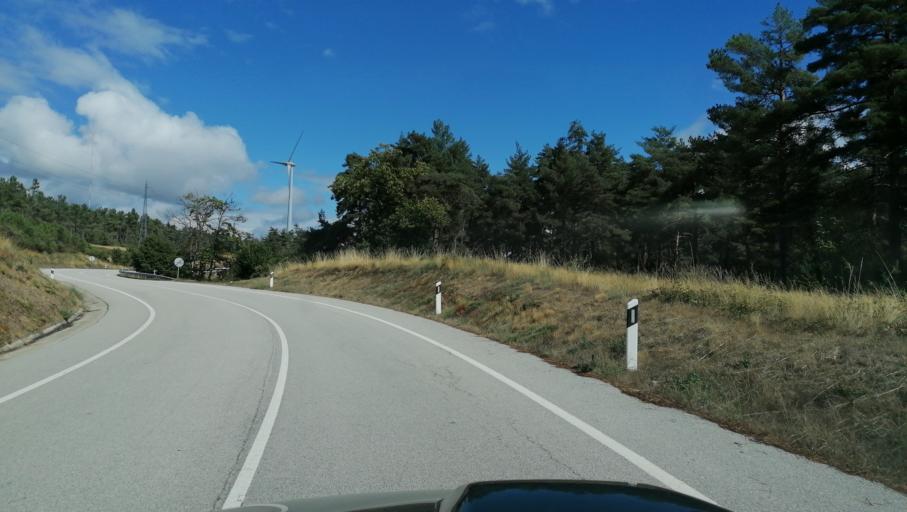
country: PT
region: Vila Real
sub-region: Vila Pouca de Aguiar
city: Vila Pouca de Aguiar
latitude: 41.5201
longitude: -7.5941
